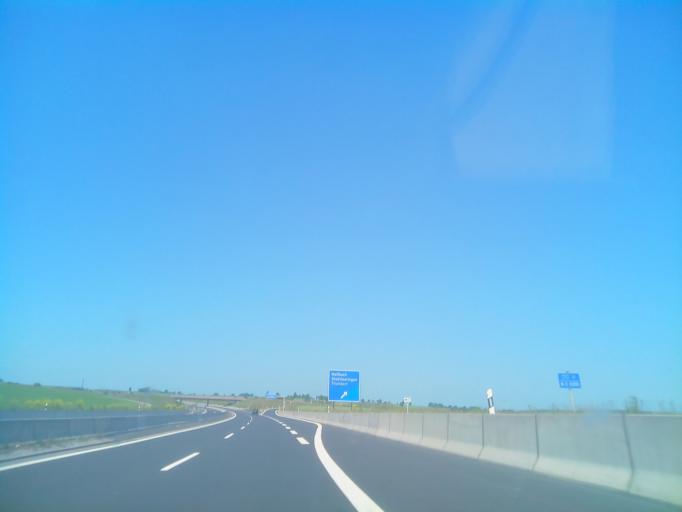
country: DE
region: Bavaria
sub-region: Regierungsbezirk Unterfranken
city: Rannungen
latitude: 50.1962
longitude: 10.2132
